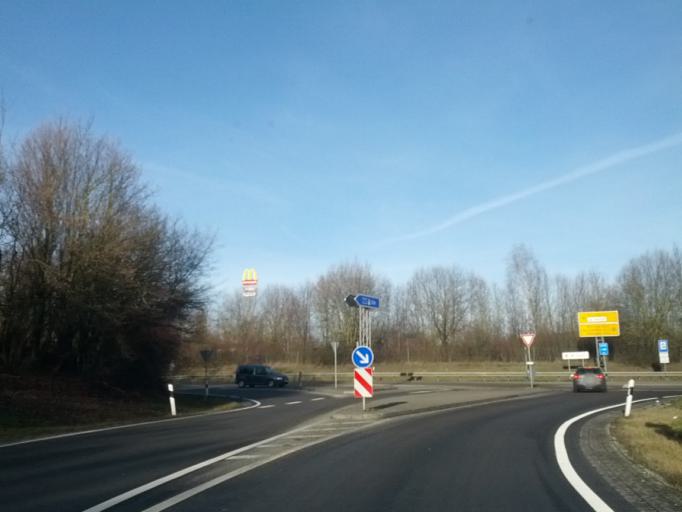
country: DE
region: Baden-Wuerttemberg
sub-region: Regierungsbezirk Stuttgart
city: Ellwangen
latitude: 48.9544
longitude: 10.1847
